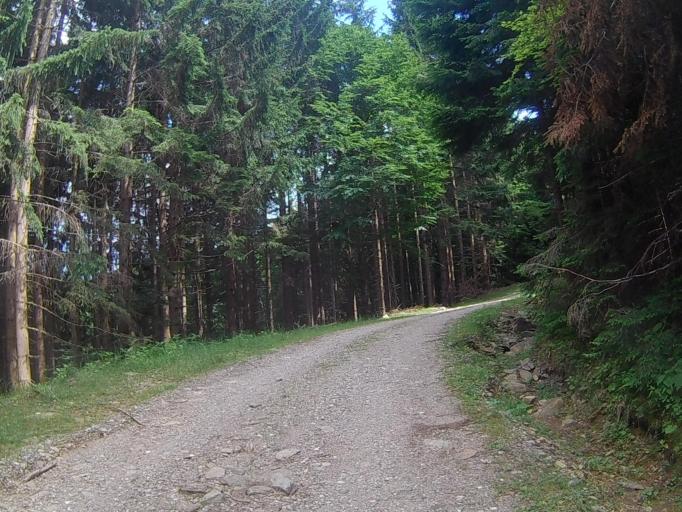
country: SI
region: Selnica ob Dravi
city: Selnica ob Dravi
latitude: 46.5084
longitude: 15.4806
